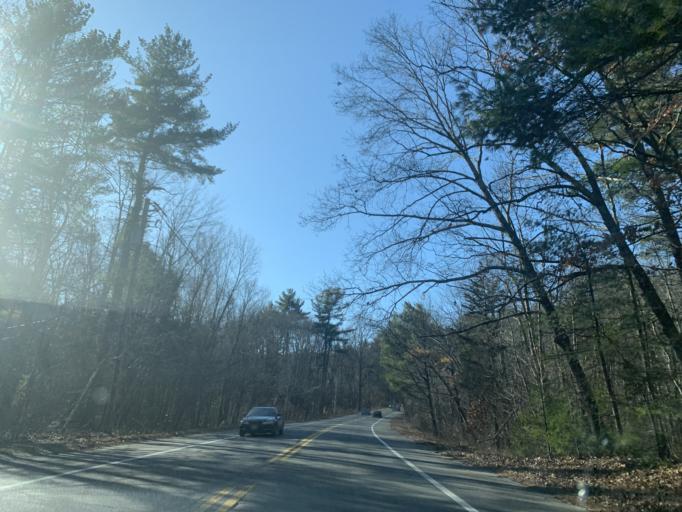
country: US
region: Massachusetts
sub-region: Middlesex County
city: Sudbury
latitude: 42.3562
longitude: -71.4648
